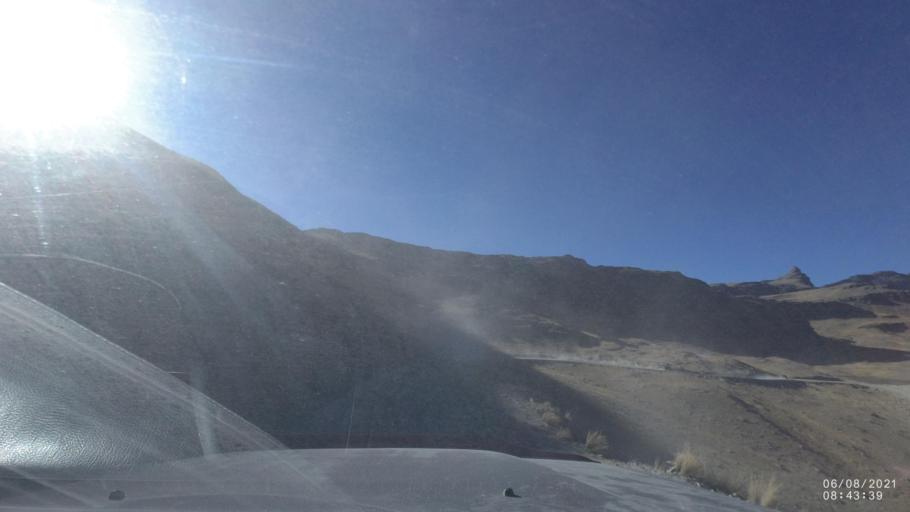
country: BO
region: Cochabamba
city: Sipe Sipe
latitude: -17.1697
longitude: -66.4106
